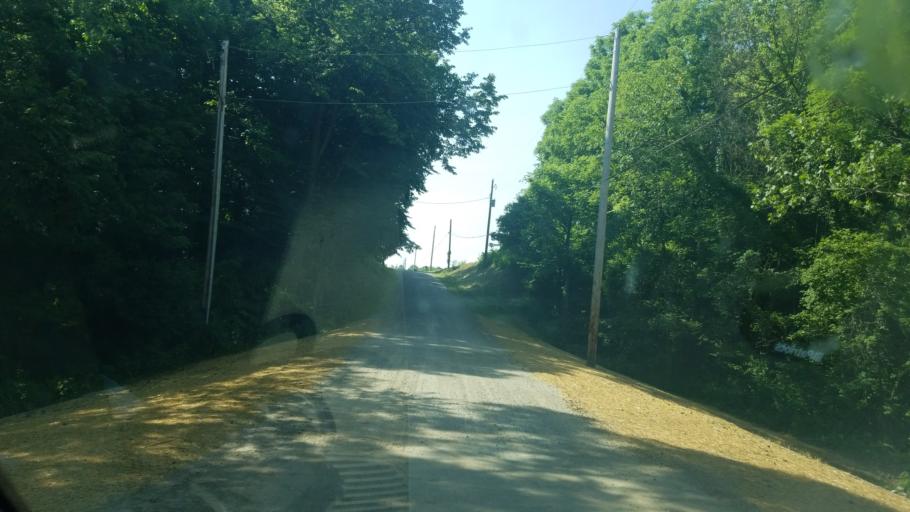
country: US
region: Ohio
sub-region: Wyandot County
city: Upper Sandusky
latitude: 40.9113
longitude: -83.2580
